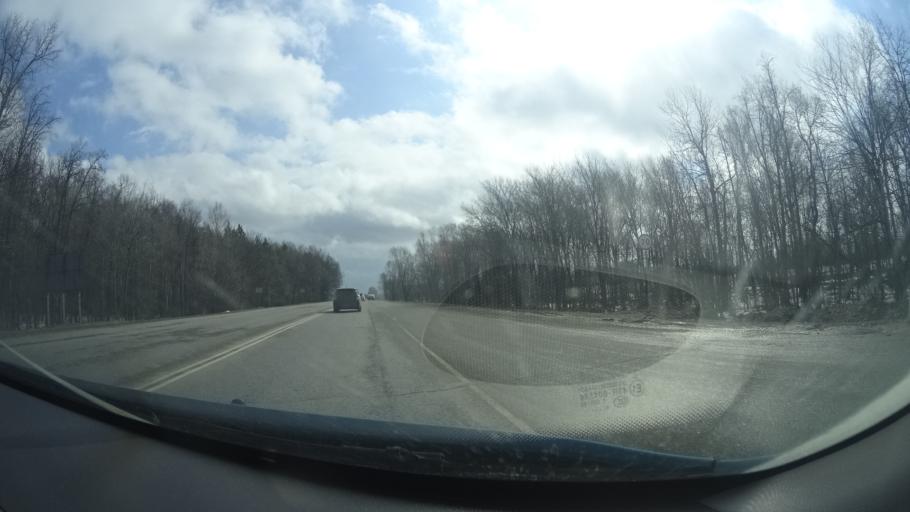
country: RU
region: Bashkortostan
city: Mikhaylovka
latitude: 54.8394
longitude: 55.7955
